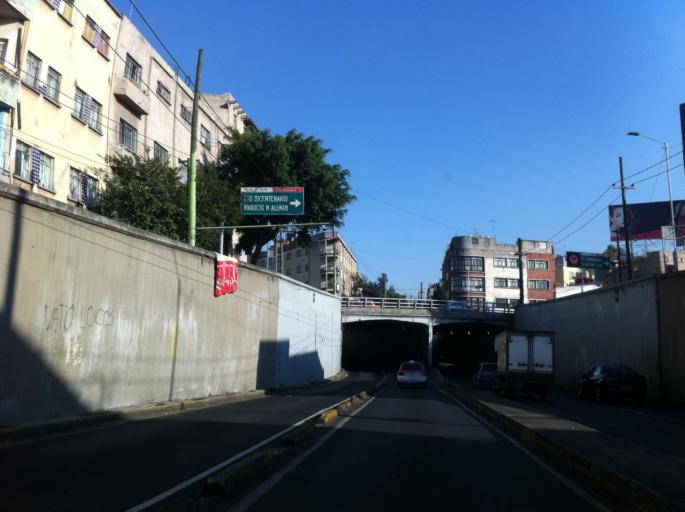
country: MX
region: Mexico City
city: Mexico City
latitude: 19.4136
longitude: -99.1357
